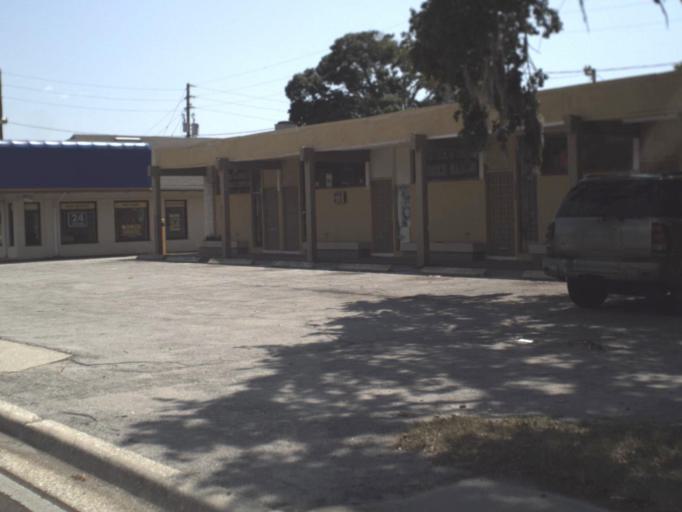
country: US
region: Florida
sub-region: Pinellas County
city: Gulfport
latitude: 27.7454
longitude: -82.6794
